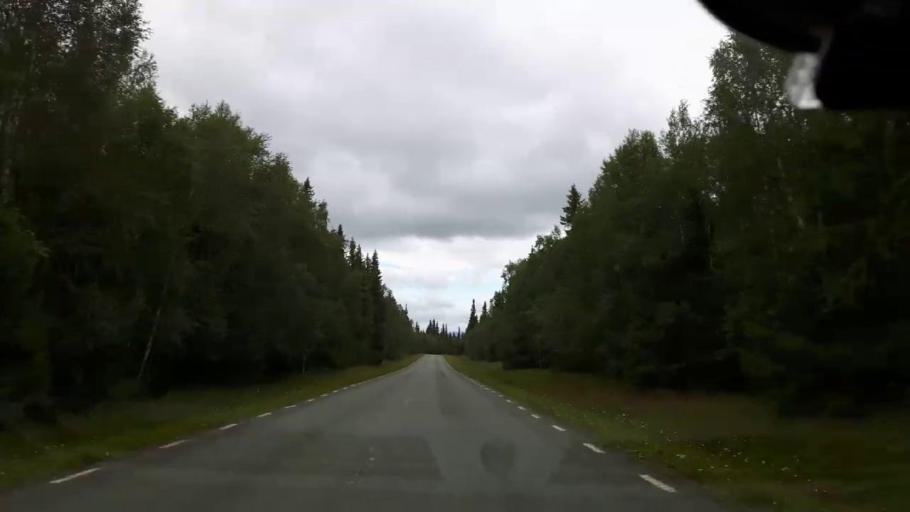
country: SE
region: Jaemtland
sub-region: Krokoms Kommun
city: Valla
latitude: 63.6078
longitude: 13.8142
